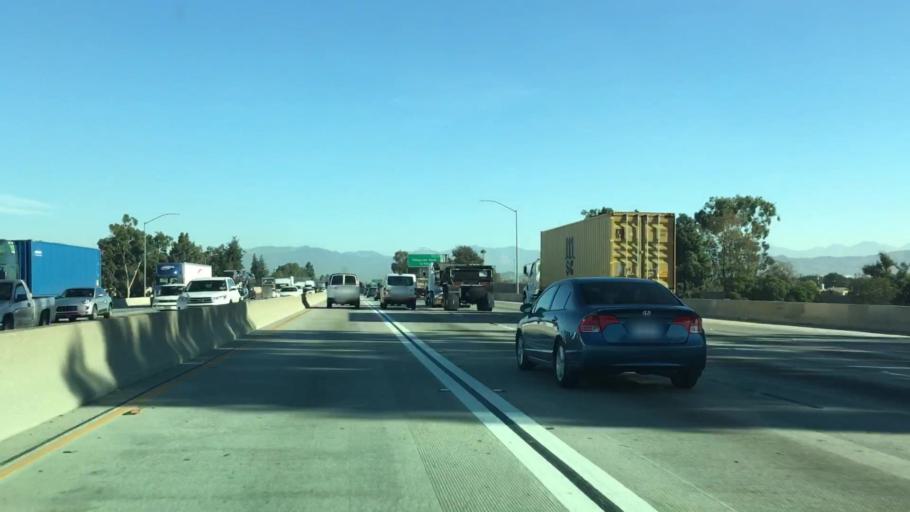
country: US
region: California
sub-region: Los Angeles County
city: Santa Fe Springs
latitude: 33.9409
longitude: -118.0967
